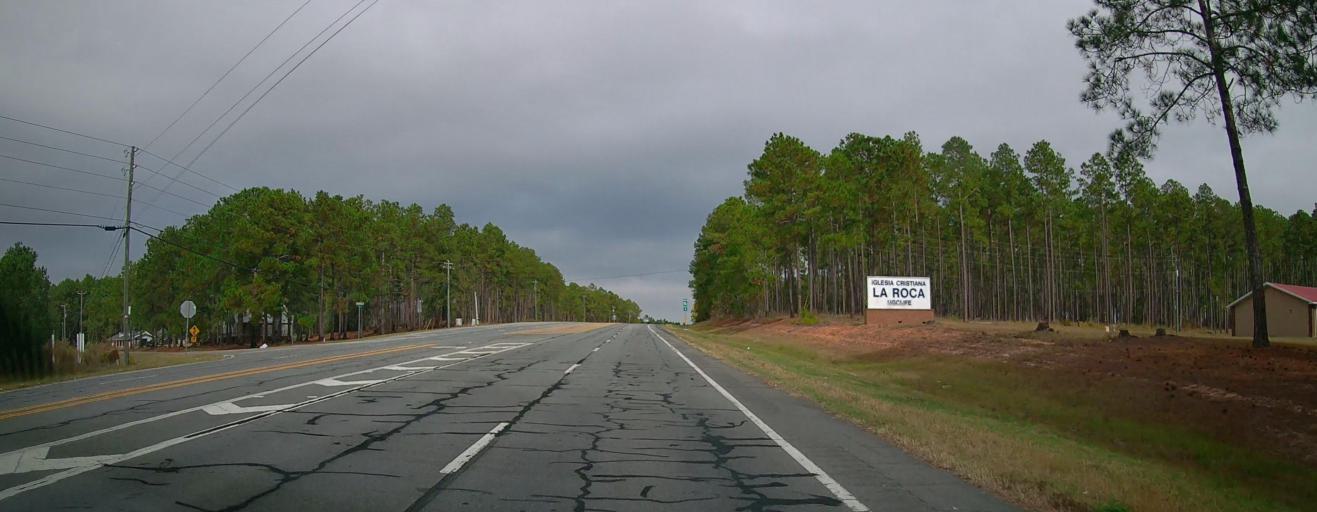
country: US
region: Georgia
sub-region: Colquitt County
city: Moultrie
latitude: 31.2274
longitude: -83.7472
